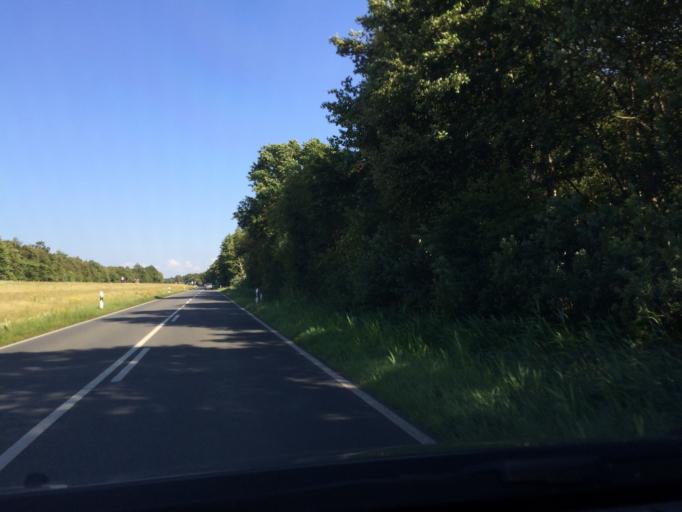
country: DE
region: Mecklenburg-Vorpommern
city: Ostseebad Prerow
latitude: 54.4463
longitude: 12.6258
